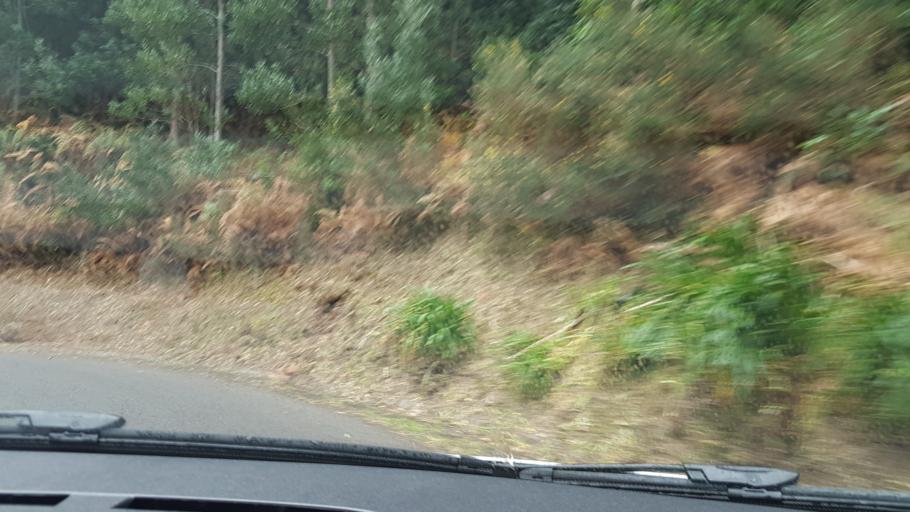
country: PT
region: Madeira
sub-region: Santa Cruz
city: Santa Cruz
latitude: 32.7274
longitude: -16.8122
